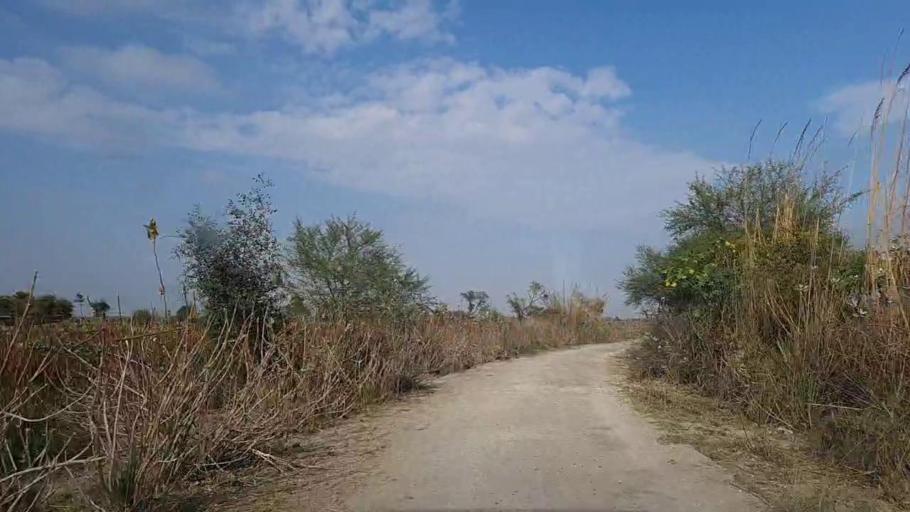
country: PK
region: Sindh
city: Sanghar
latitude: 26.2605
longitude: 69.0077
